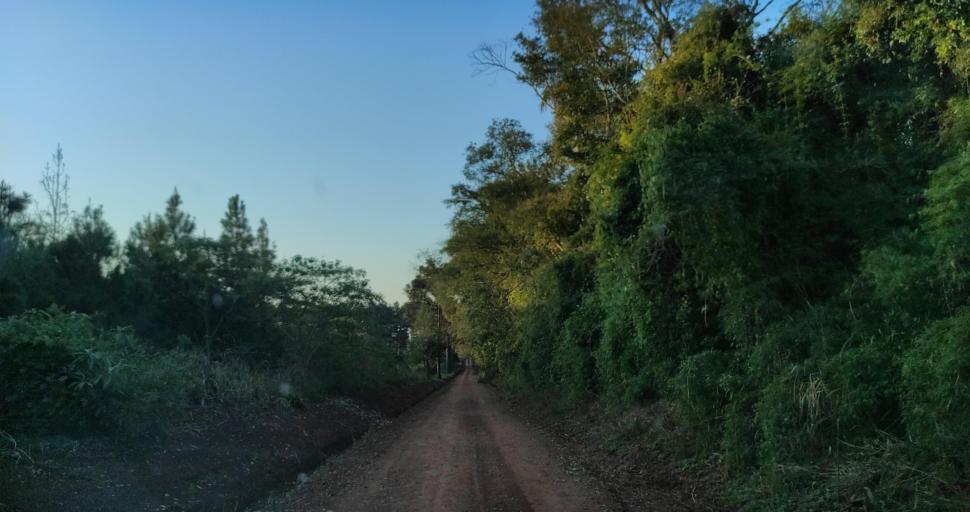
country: AR
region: Misiones
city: Capiovi
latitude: -26.8798
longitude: -55.1077
